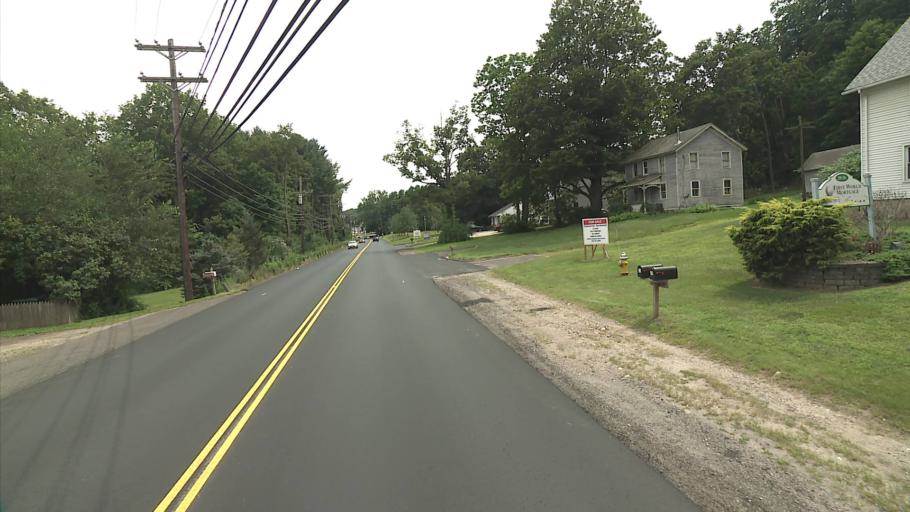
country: US
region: Connecticut
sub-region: New Haven County
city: Seymour
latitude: 41.4022
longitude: -73.0907
